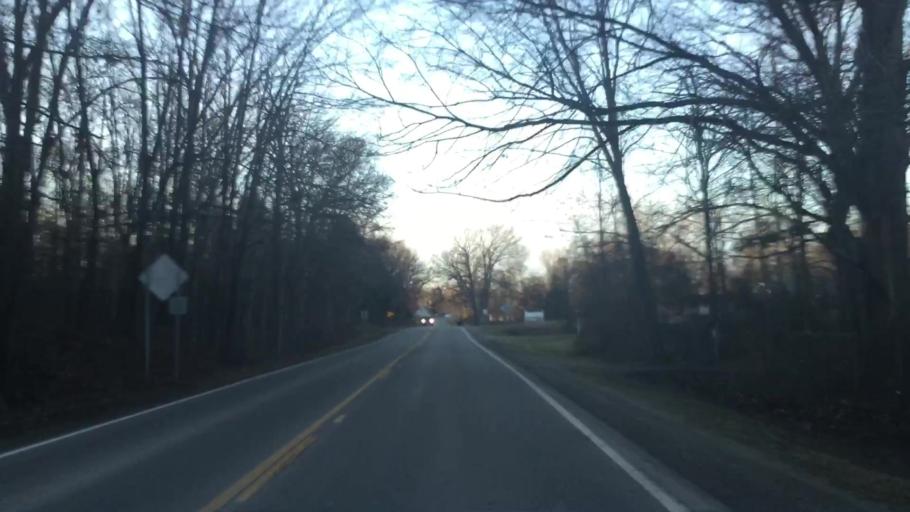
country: US
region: Michigan
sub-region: Genesee County
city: Argentine
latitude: 42.8078
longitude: -83.8409
